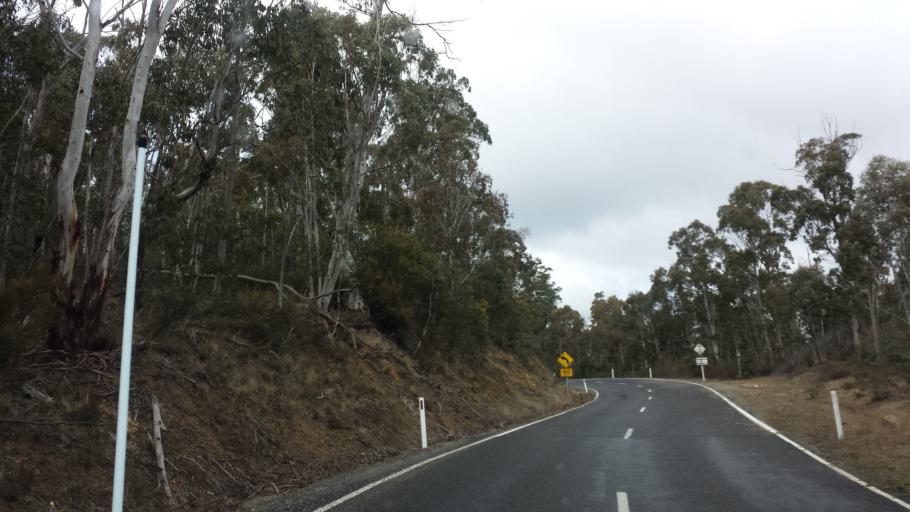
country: AU
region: Victoria
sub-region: Alpine
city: Mount Beauty
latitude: -37.1325
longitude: 147.5008
